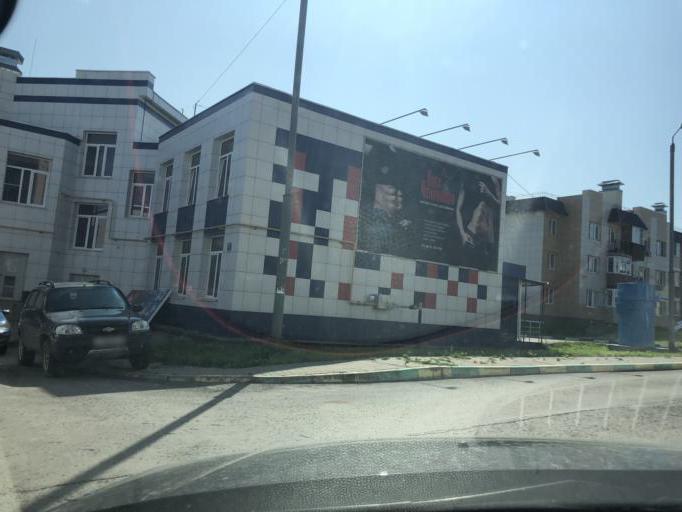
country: RU
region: Tula
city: Tula
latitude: 54.1752
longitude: 37.6568
